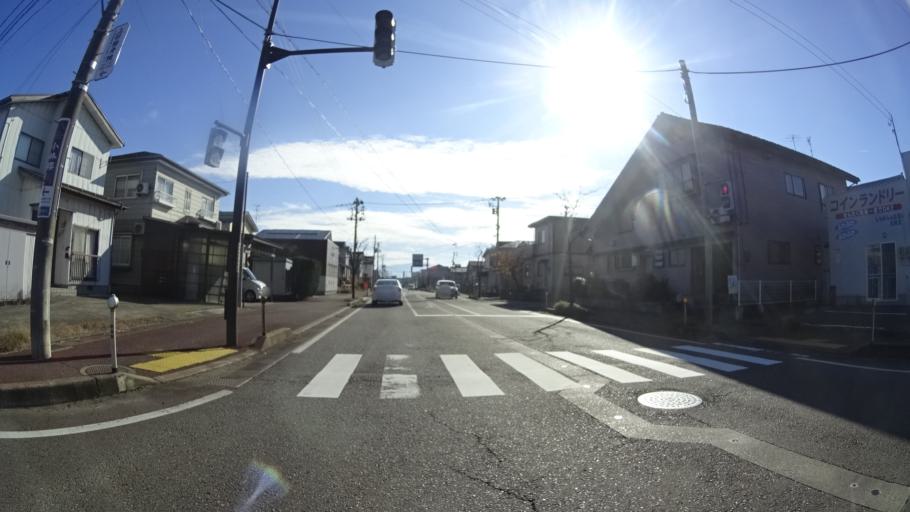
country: JP
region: Niigata
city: Mitsuke
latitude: 37.5439
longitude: 138.8858
